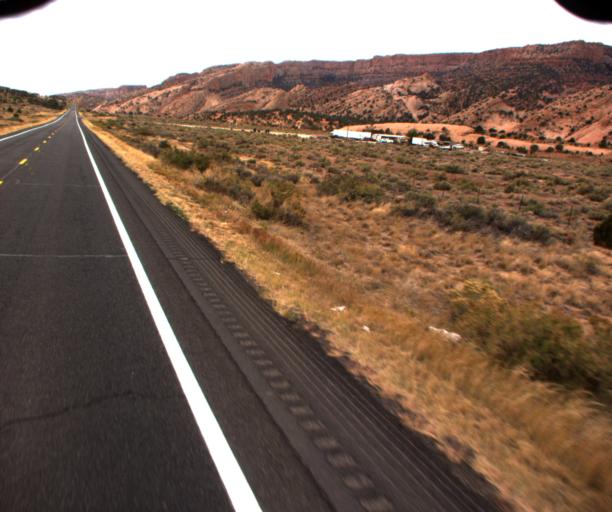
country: US
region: Arizona
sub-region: Navajo County
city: Kayenta
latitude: 36.6711
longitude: -110.4029
